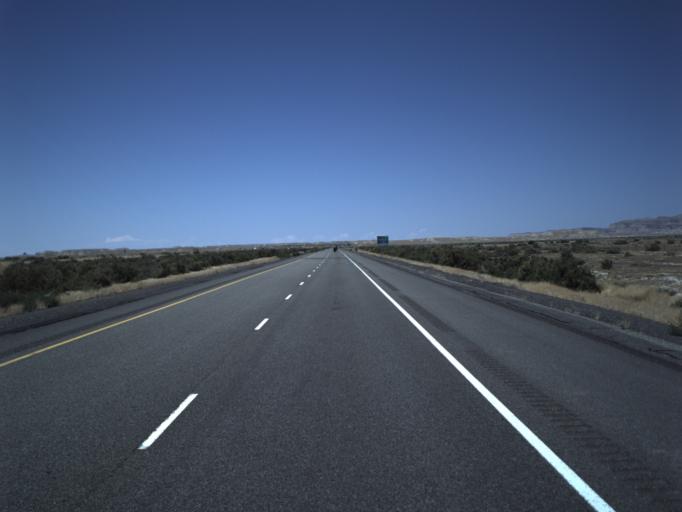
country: US
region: Utah
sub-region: Grand County
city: Moab
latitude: 38.9428
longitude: -109.5877
